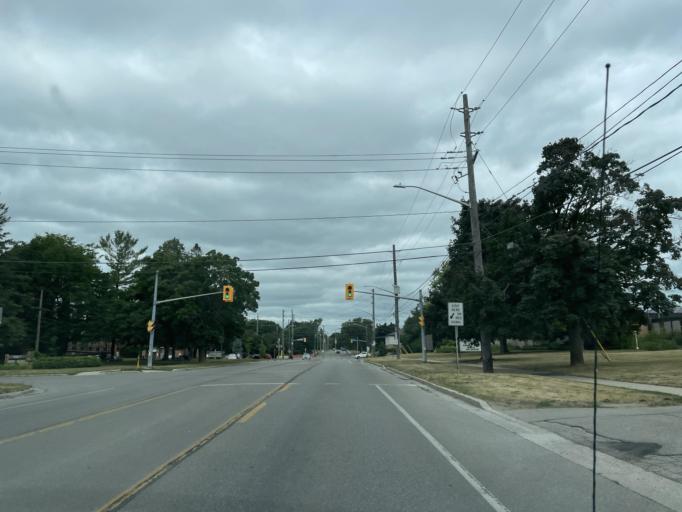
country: CA
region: Ontario
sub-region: Wellington County
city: Guelph
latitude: 43.5648
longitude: -80.2560
